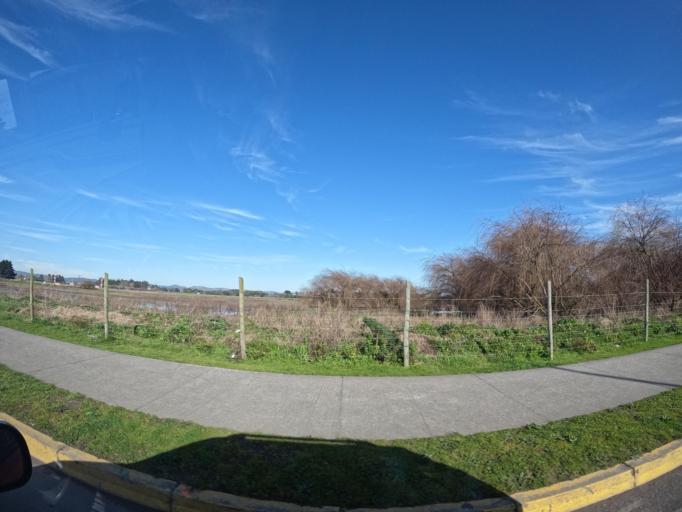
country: CL
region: Biobio
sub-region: Provincia de Concepcion
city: Concepcion
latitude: -36.7776
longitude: -73.0730
